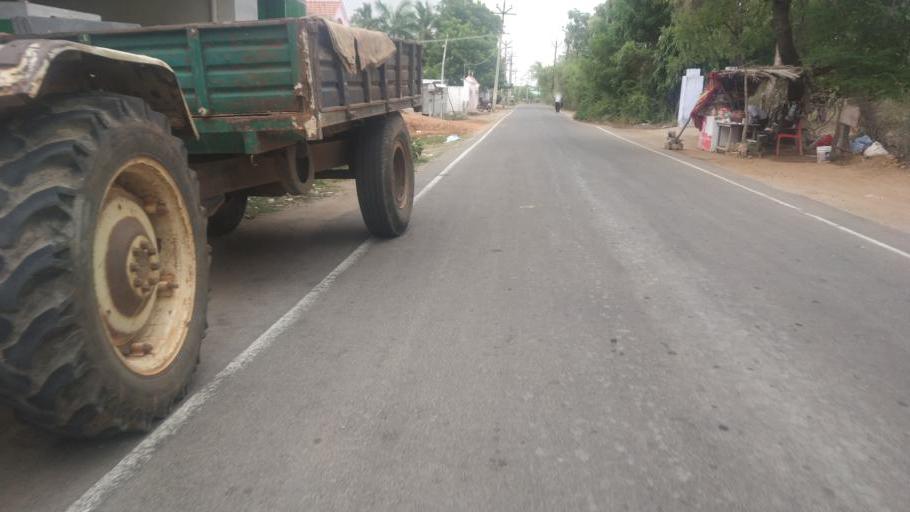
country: IN
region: Tamil Nadu
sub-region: Tirunelveli Kattabo
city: Tirunelveli
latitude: 8.6883
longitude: 77.7251
